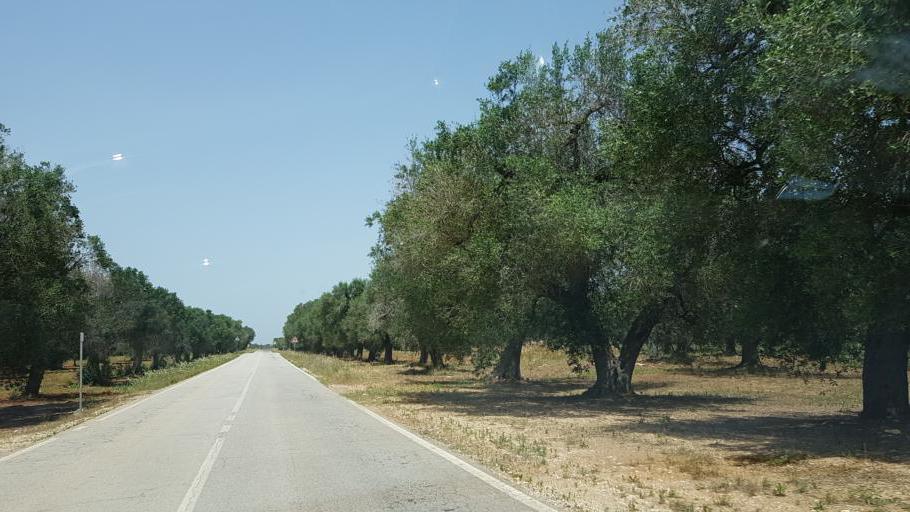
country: IT
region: Apulia
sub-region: Provincia di Brindisi
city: San Pancrazio Salentino
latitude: 40.4573
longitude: 17.8397
